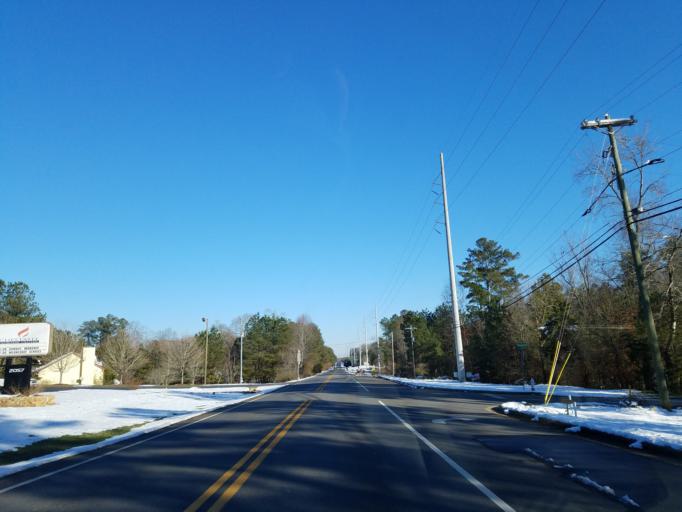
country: US
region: Georgia
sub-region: Dawson County
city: Dawsonville
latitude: 34.3538
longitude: -84.0801
